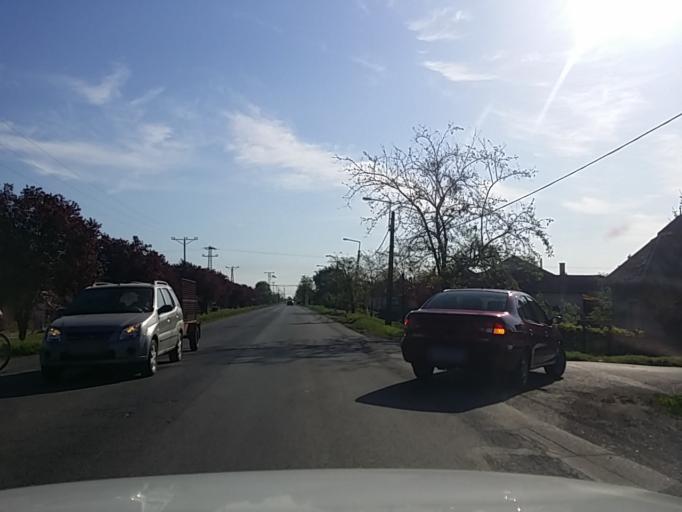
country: HU
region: Jasz-Nagykun-Szolnok
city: Mezotur
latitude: 47.0013
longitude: 20.6372
